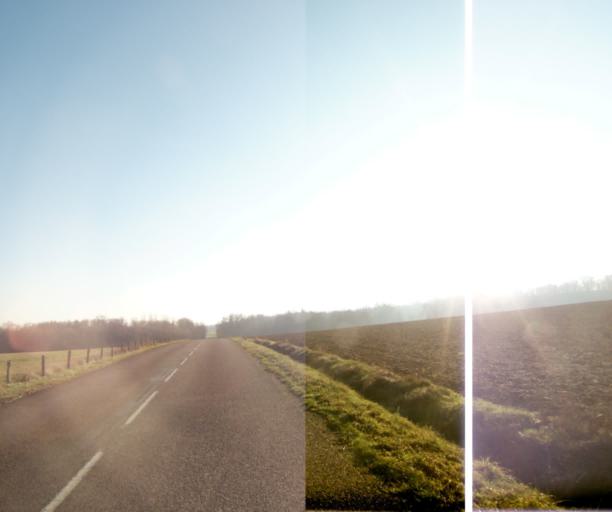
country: FR
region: Champagne-Ardenne
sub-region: Departement de la Haute-Marne
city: Bienville
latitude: 48.5946
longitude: 5.0801
